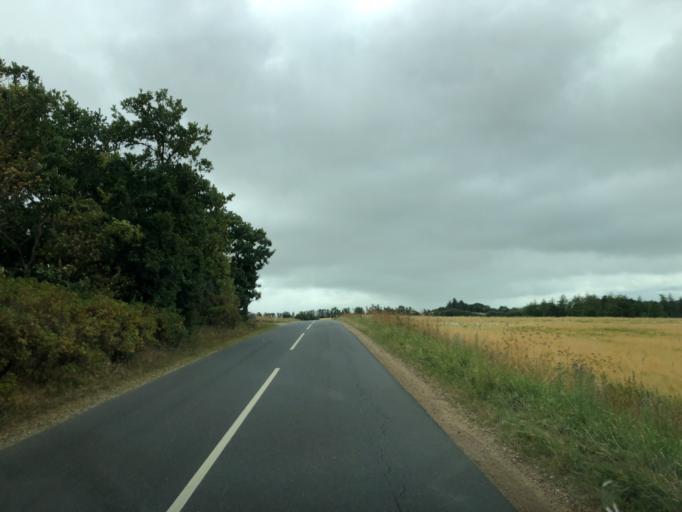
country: DK
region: Central Jutland
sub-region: Herning Kommune
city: Vildbjerg
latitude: 56.2289
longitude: 8.6426
